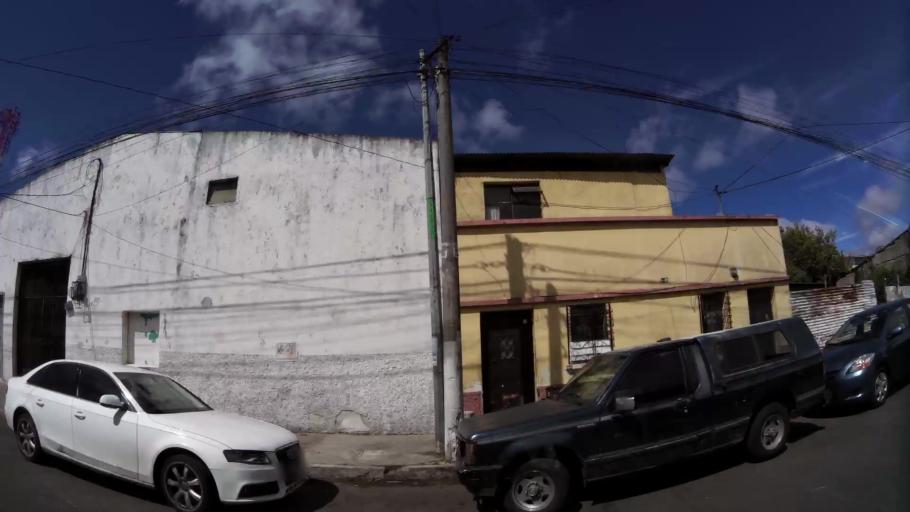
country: GT
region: Guatemala
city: Guatemala City
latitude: 14.6077
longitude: -90.5355
